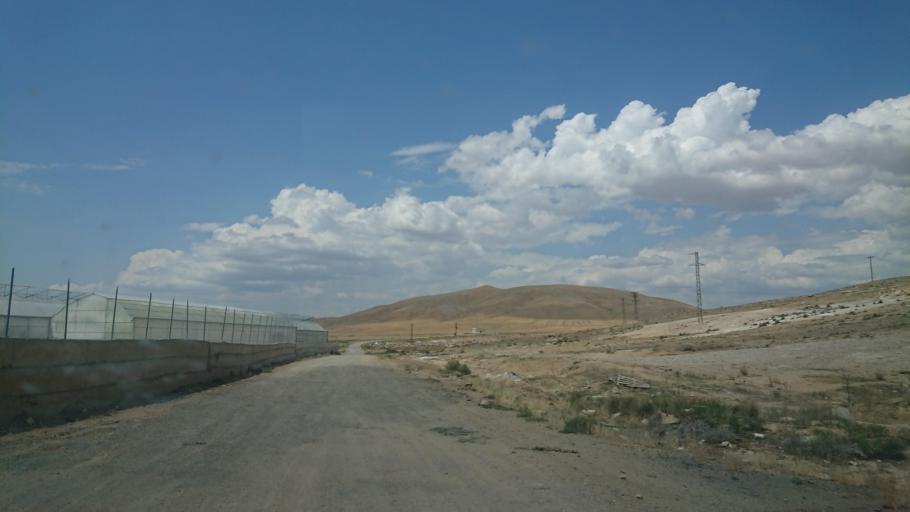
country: TR
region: Aksaray
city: Sariyahsi
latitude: 39.0010
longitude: 33.9116
